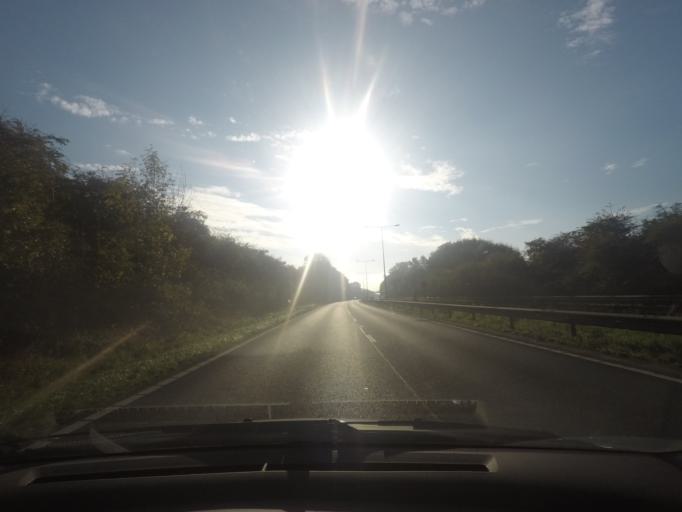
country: GB
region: England
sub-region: East Riding of Yorkshire
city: Brantingham
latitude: 53.7444
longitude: -0.5684
